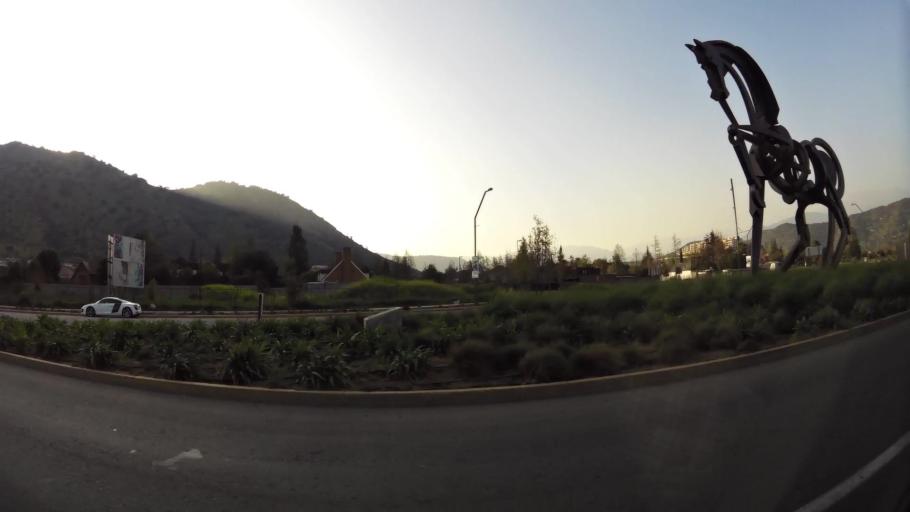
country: CL
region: Santiago Metropolitan
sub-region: Provincia de Santiago
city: Villa Presidente Frei, Nunoa, Santiago, Chile
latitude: -33.3584
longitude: -70.5429
